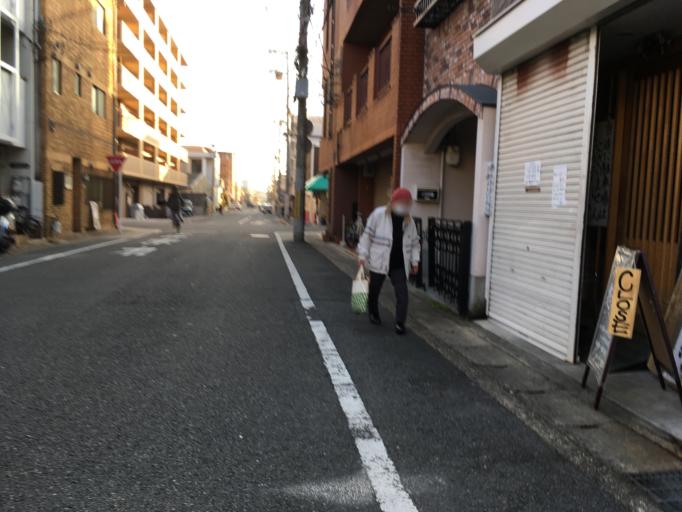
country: JP
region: Kyoto
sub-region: Kyoto-shi
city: Kamigyo-ku
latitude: 35.0443
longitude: 135.7859
